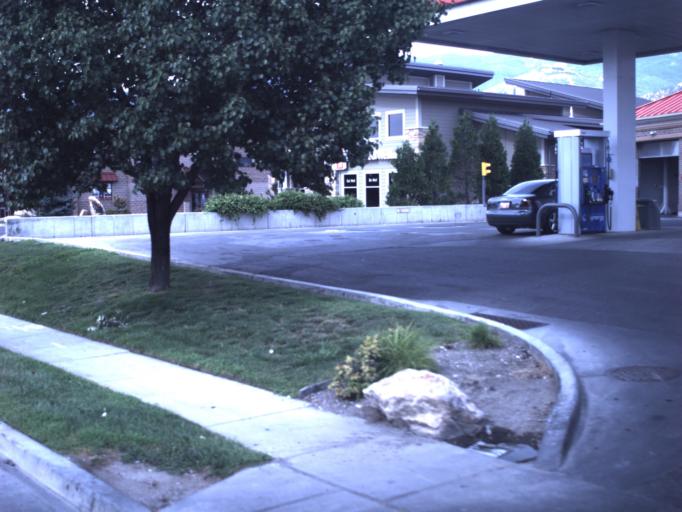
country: US
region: Utah
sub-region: Davis County
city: West Bountiful
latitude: 40.8945
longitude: -111.8921
